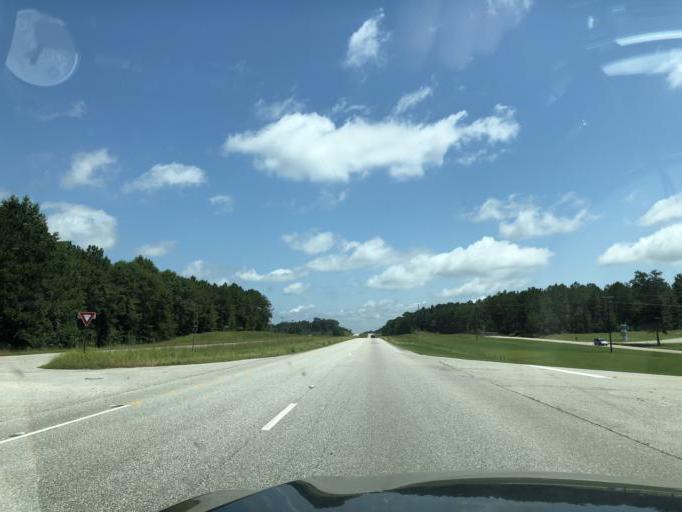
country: US
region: Alabama
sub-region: Barbour County
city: Eufaula
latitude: 31.7502
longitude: -85.2270
